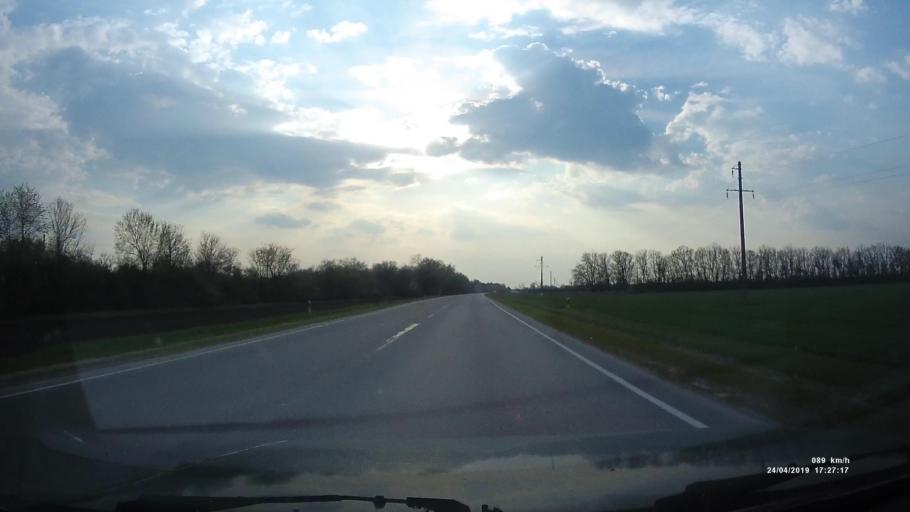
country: RU
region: Rostov
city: Gigant
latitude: 46.5285
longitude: 41.2043
